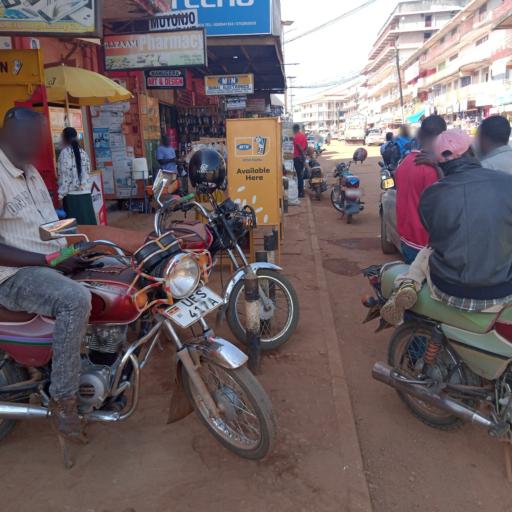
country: UG
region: Central Region
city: Masaka
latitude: -0.3406
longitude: 31.7378
